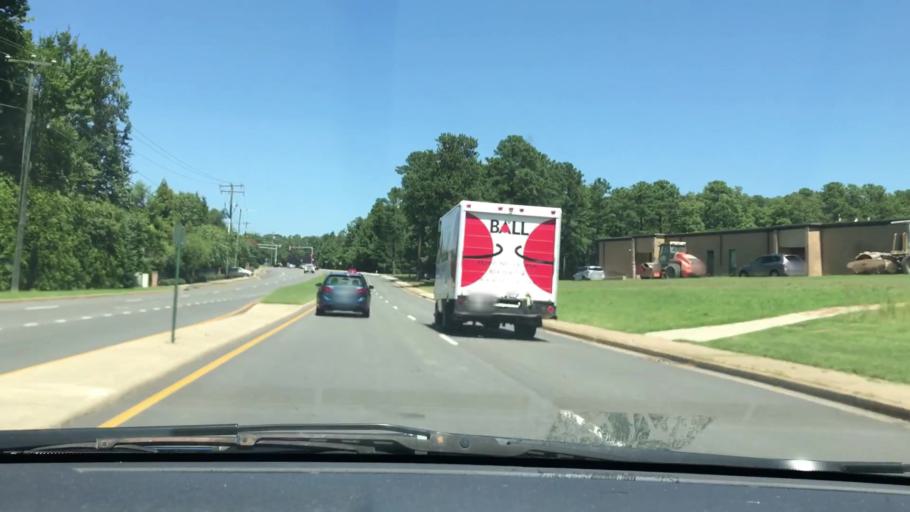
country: US
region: Virginia
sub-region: Henrico County
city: Short Pump
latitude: 37.6196
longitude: -77.6064
